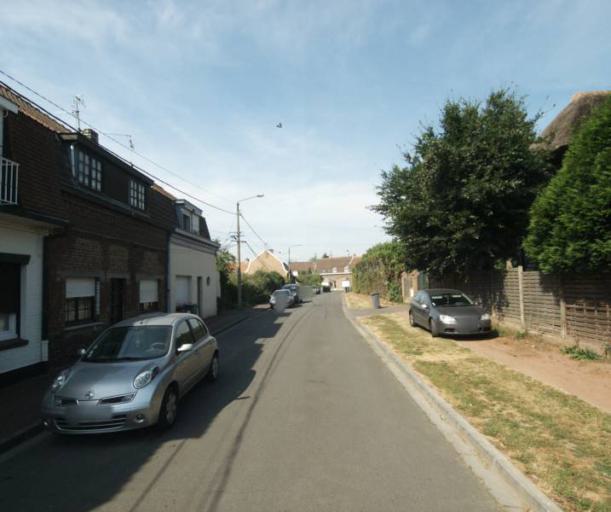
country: FR
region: Nord-Pas-de-Calais
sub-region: Departement du Nord
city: Mouvaux
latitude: 50.7126
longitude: 3.1348
